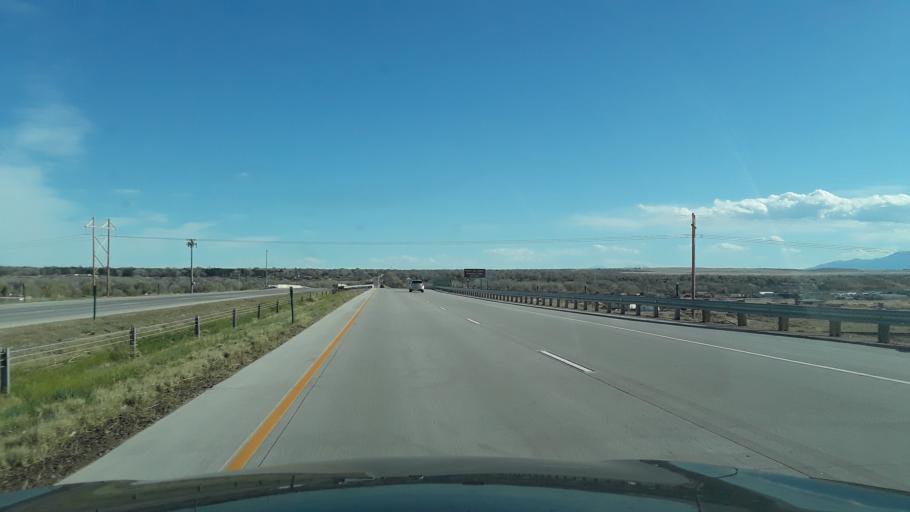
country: US
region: Colorado
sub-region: Pueblo County
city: Pueblo
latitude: 38.2836
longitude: -104.6633
